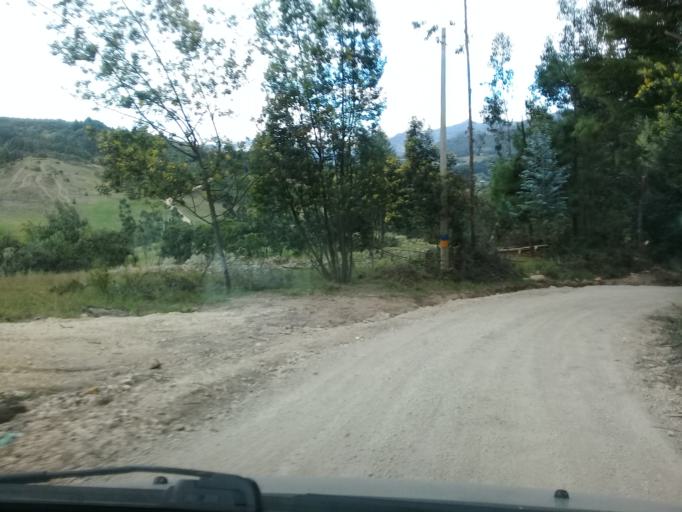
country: CO
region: Cundinamarca
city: Lenguazaque
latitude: 5.2906
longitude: -73.7244
